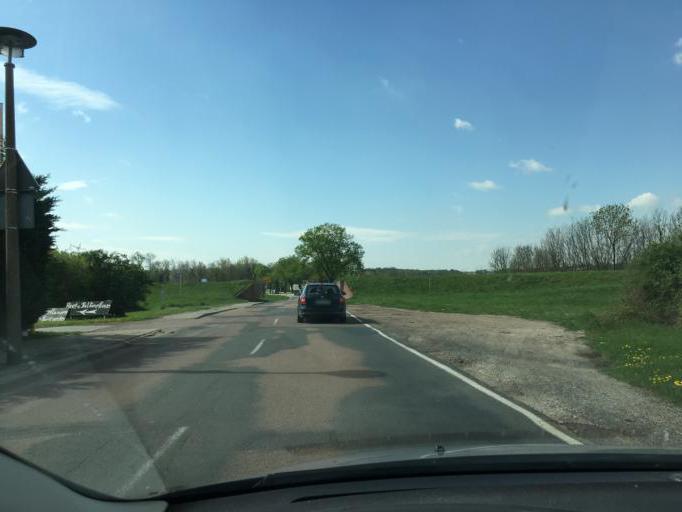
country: DE
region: Saxony-Anhalt
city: Beesenlaublingen
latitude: 51.7064
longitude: 11.6927
